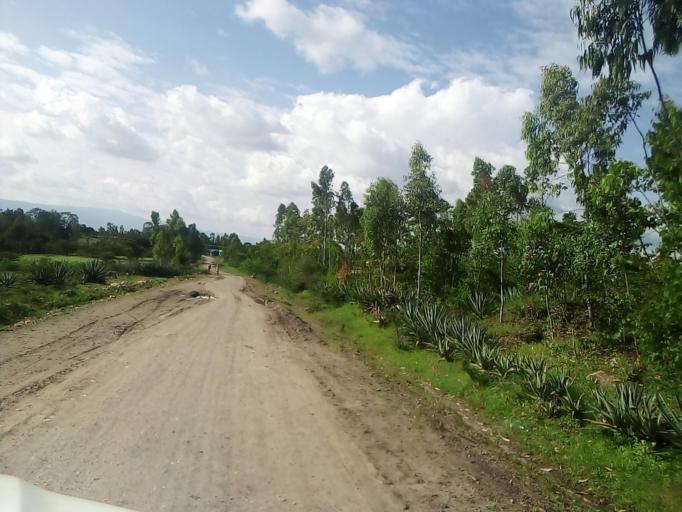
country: ET
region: Southern Nations, Nationalities, and People's Region
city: K'olito
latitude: 7.6363
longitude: 38.0599
